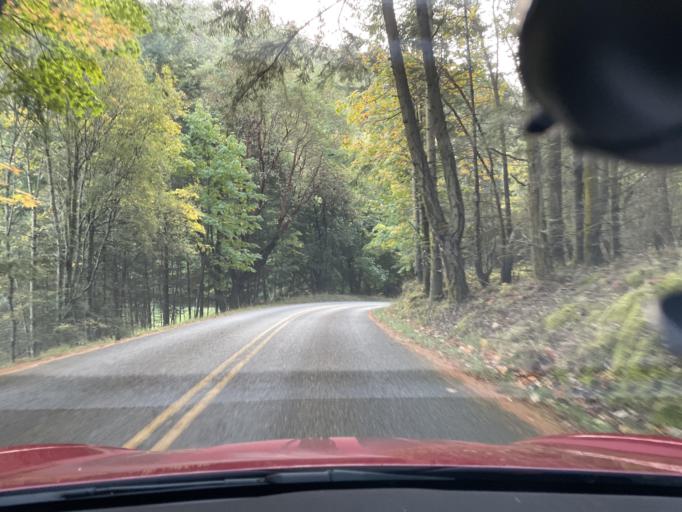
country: US
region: Washington
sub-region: San Juan County
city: Friday Harbor
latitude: 48.5190
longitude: -123.1423
